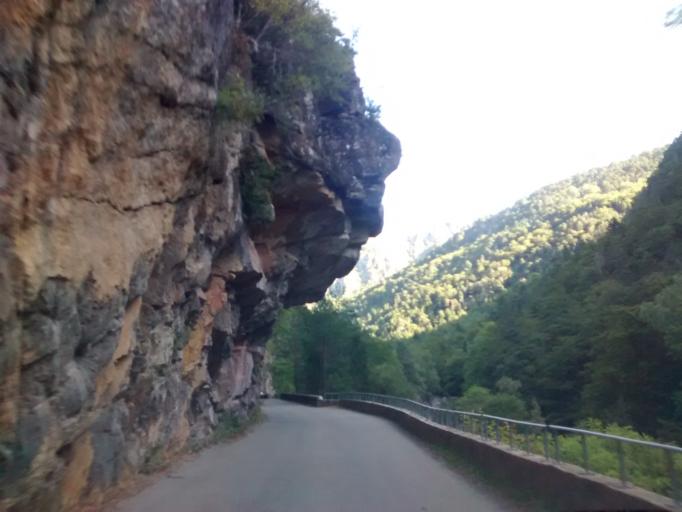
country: ES
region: Aragon
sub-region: Provincia de Huesca
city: Aragues del Puerto
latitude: 42.8073
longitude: -0.7139
